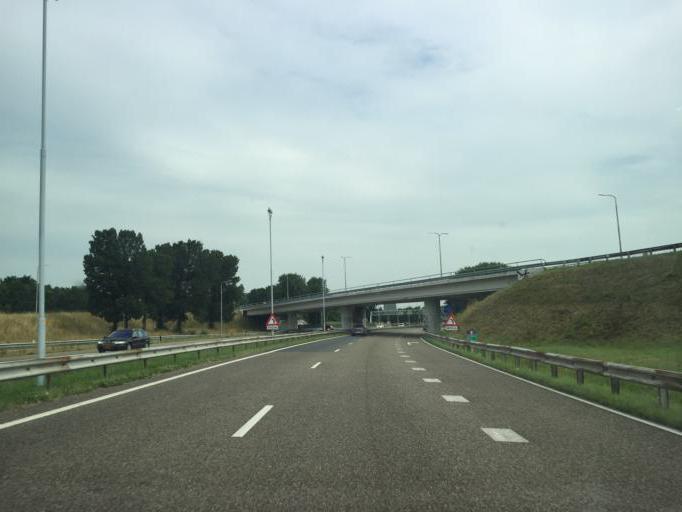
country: NL
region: North Holland
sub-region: Gemeente Velsen
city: Velsen-Zuid
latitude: 52.4481
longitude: 4.6551
